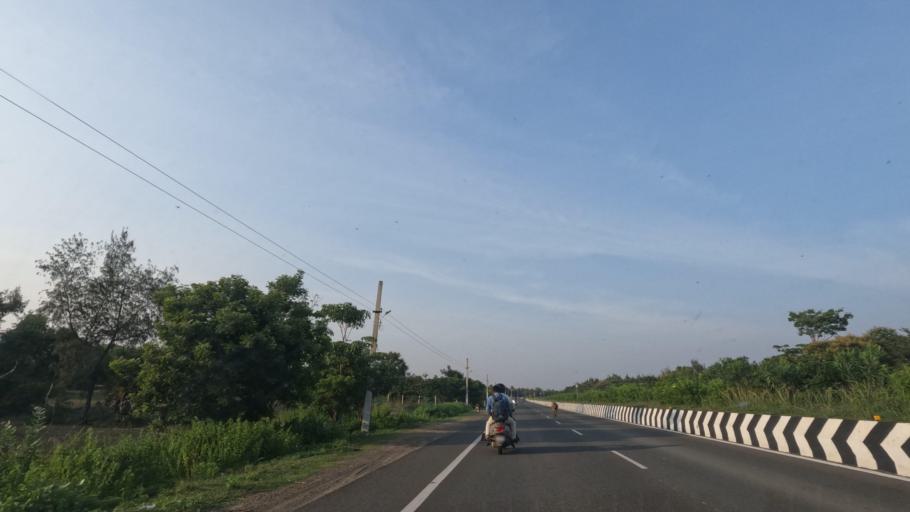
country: IN
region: Tamil Nadu
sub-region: Kancheepuram
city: Mamallapuram
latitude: 12.6639
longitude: 80.2094
